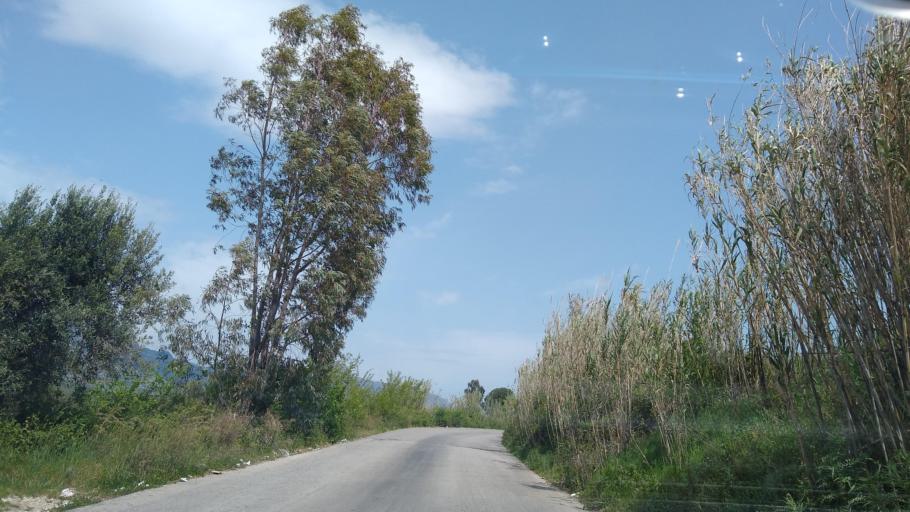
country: IT
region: Sicily
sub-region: Palermo
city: San Cipirello
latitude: 37.9622
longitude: 13.1331
